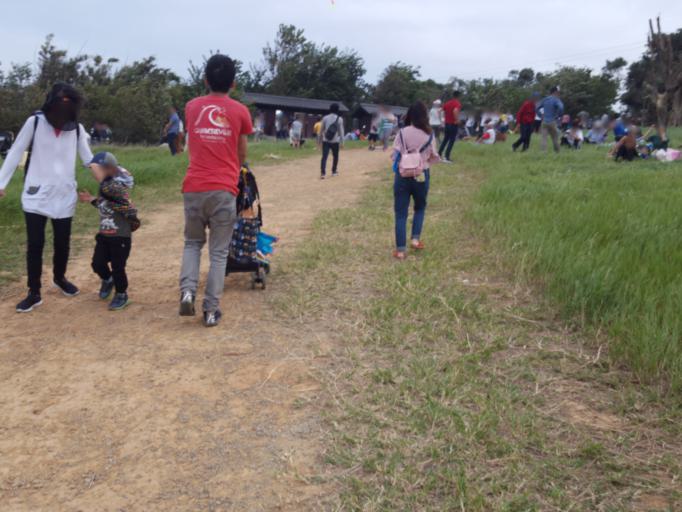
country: TW
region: Taiwan
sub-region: Hsinchu
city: Hsinchu
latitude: 24.7733
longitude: 120.9258
